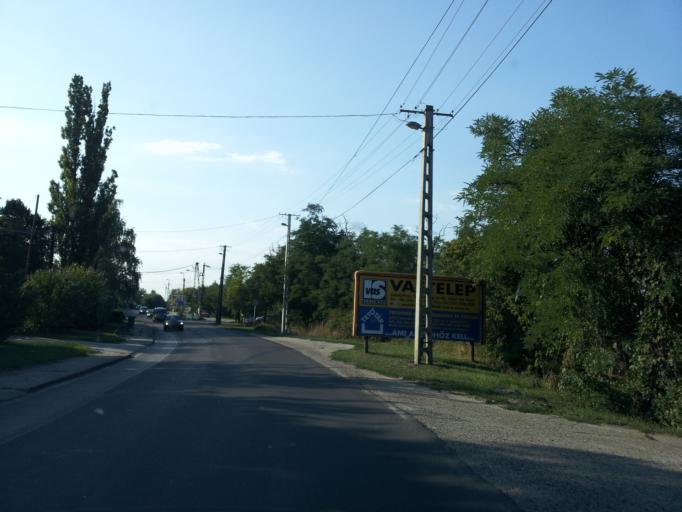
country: HU
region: Pest
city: Tahitotfalu
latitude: 47.7415
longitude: 19.0858
